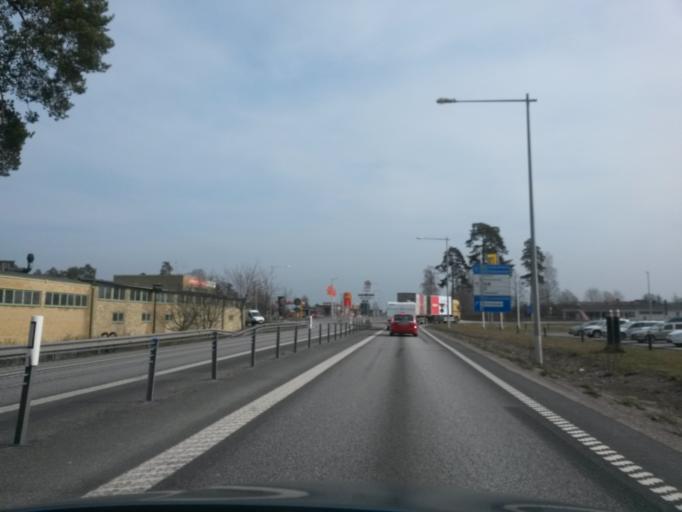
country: SE
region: OErebro
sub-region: Laxa Kommun
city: Laxa
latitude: 58.9813
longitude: 14.6221
